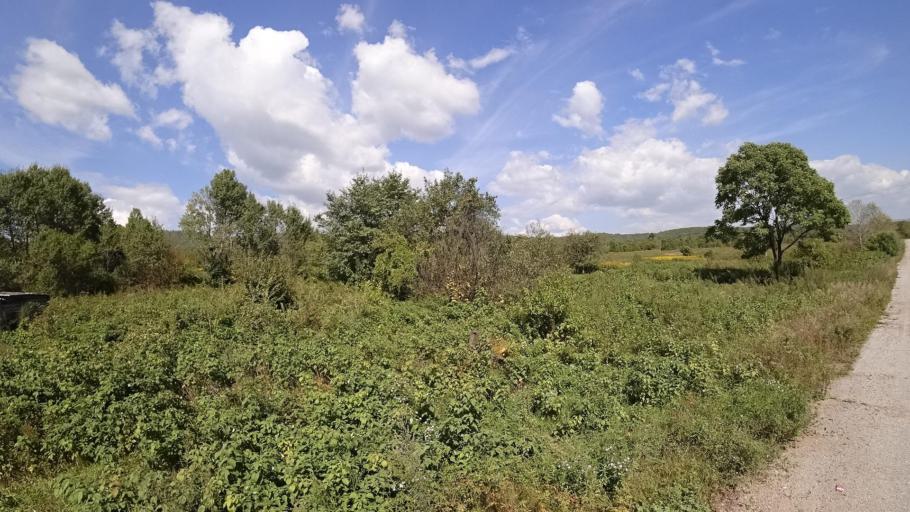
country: RU
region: Jewish Autonomous Oblast
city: Londoko
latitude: 49.0113
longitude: 131.9552
